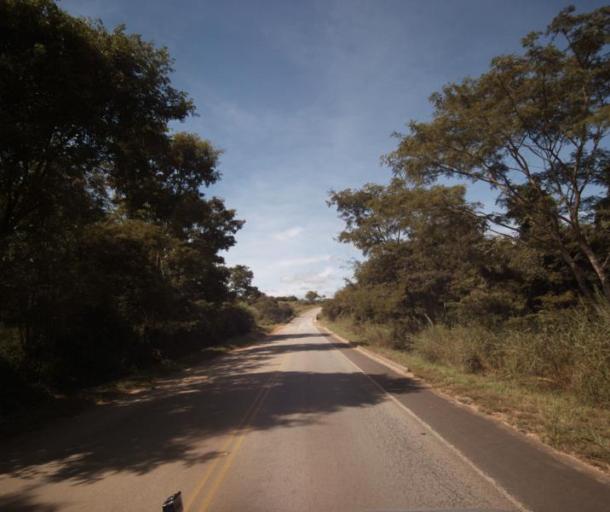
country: BR
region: Goias
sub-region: Abadiania
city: Abadiania
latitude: -16.1366
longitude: -48.8919
